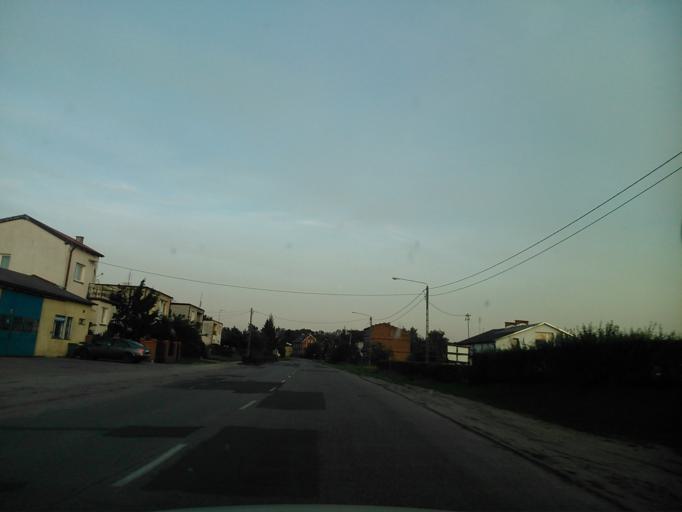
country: PL
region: Kujawsko-Pomorskie
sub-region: Powiat wabrzeski
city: Wabrzezno
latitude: 53.2680
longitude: 18.9771
